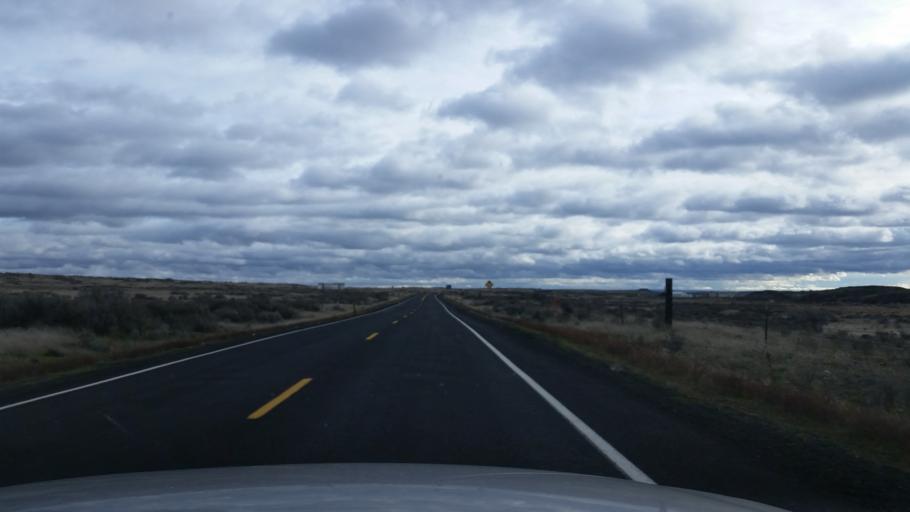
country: US
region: Washington
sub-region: Lincoln County
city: Davenport
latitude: 47.3190
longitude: -117.9770
